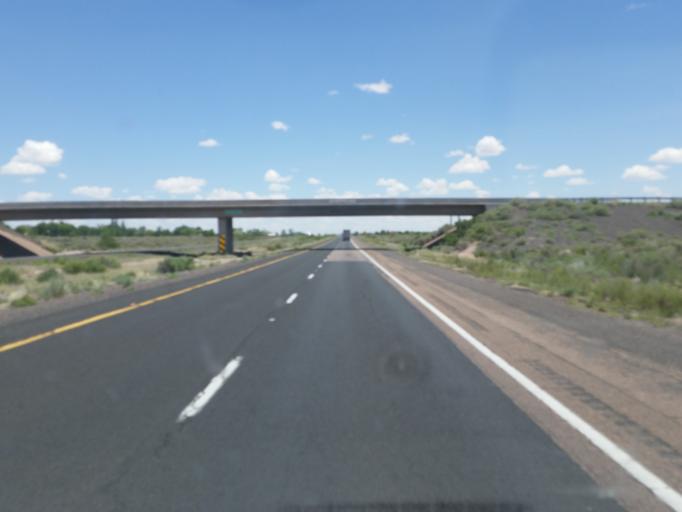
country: US
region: Arizona
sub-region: Navajo County
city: Joseph City
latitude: 34.9563
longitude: -110.3526
